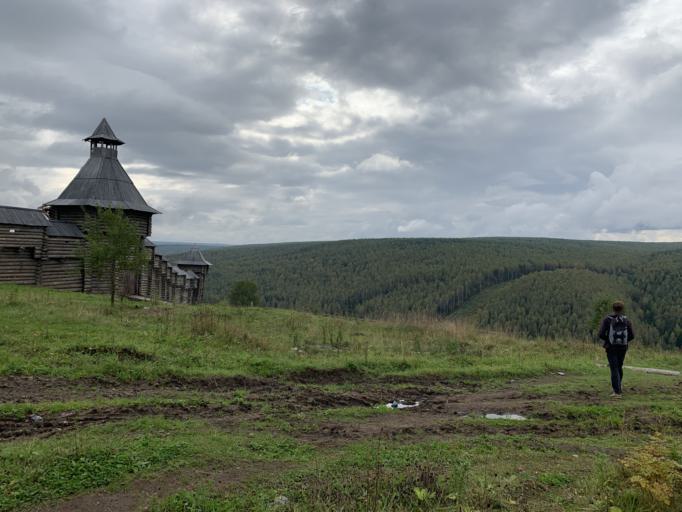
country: RU
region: Perm
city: Gubakha
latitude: 58.8701
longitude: 57.6281
